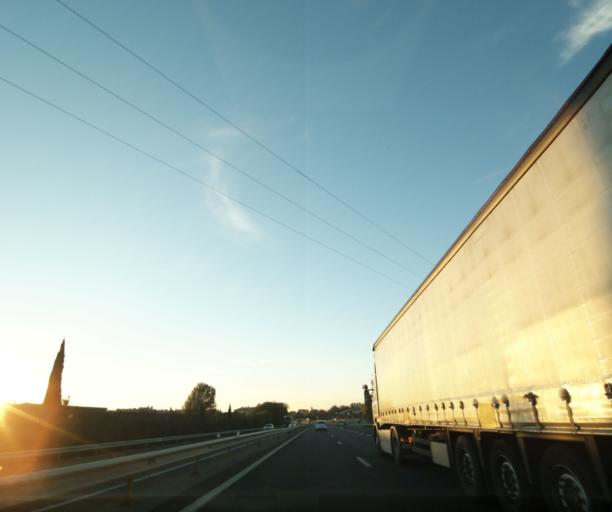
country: FR
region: Provence-Alpes-Cote d'Azur
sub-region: Departement des Bouches-du-Rhone
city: Salon-de-Provence
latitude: 43.6269
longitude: 5.1146
